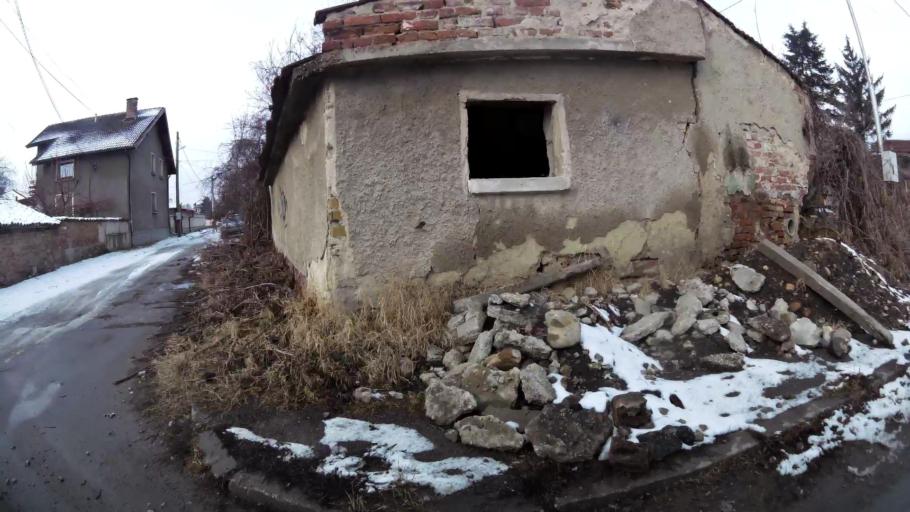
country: BG
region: Sofia-Capital
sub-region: Stolichna Obshtina
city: Sofia
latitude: 42.7140
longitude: 23.4200
